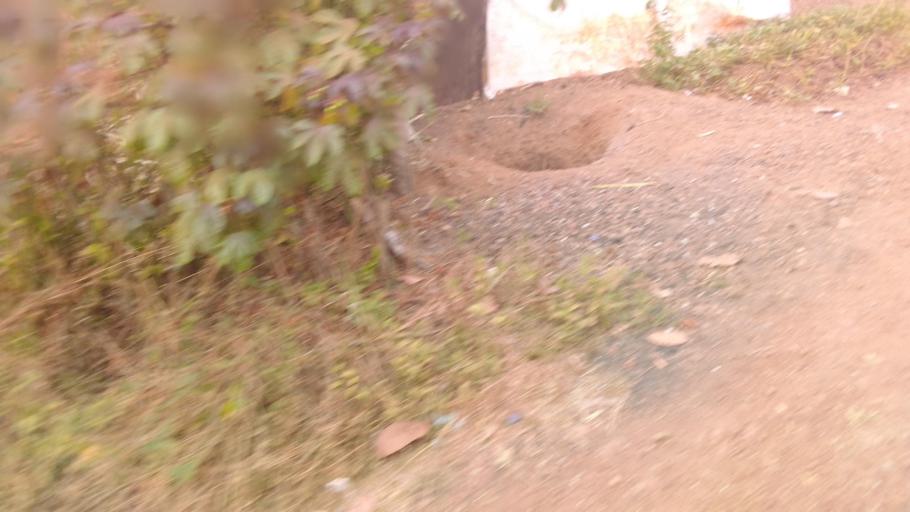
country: SL
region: Southern Province
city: Mogbwemo
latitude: 7.7582
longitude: -12.3041
